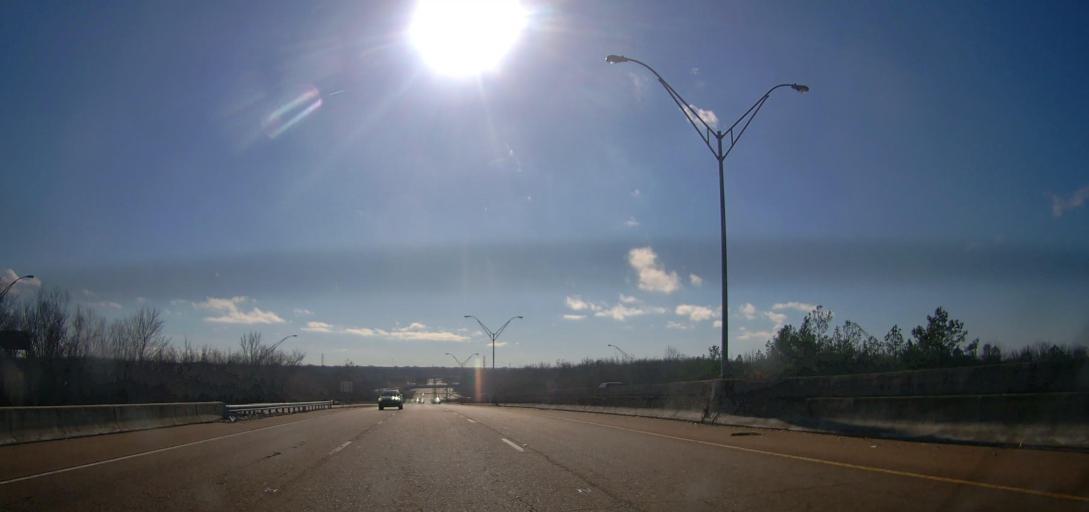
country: US
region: Tennessee
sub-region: Shelby County
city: Bartlett
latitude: 35.2042
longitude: -89.9236
